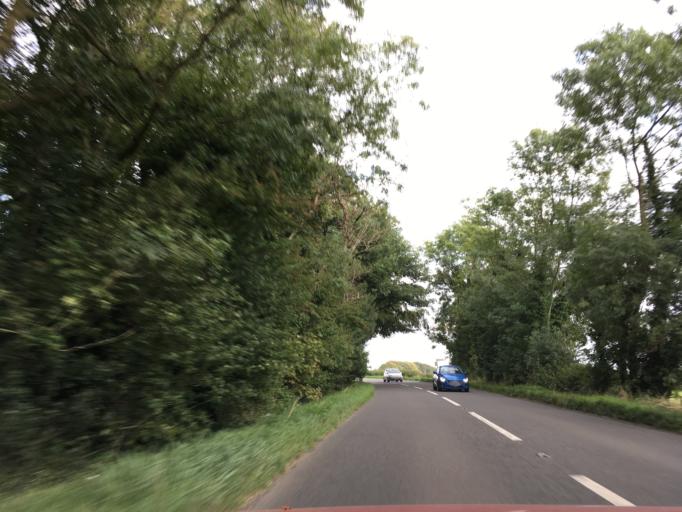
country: GB
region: England
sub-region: Gloucestershire
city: Dursley
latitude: 51.6672
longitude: -2.2919
